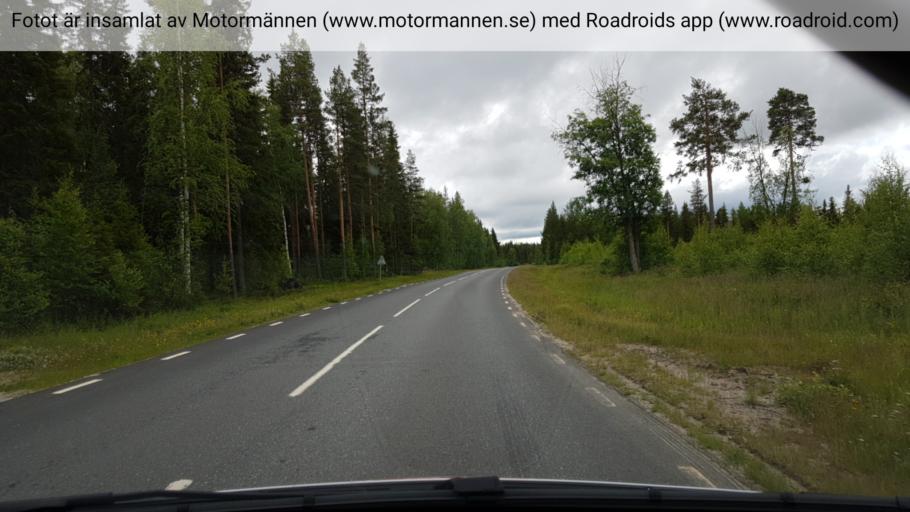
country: SE
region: Vaesterbotten
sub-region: Norsjo Kommun
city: Norsjoe
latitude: 64.6401
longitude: 19.2855
